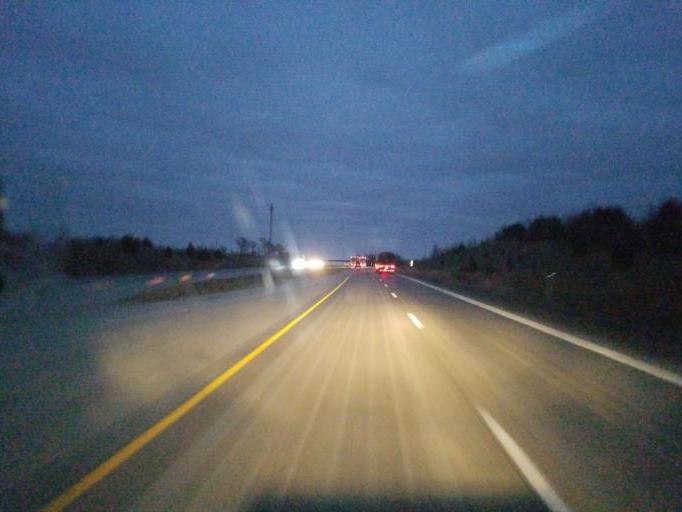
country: US
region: Iowa
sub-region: Cass County
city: Atlantic
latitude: 41.4962
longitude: -94.7848
